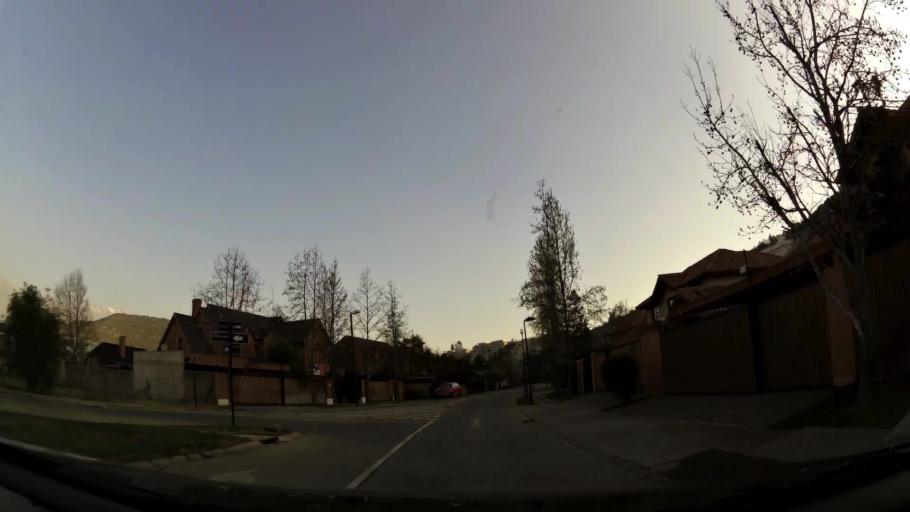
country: CL
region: Santiago Metropolitan
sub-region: Provincia de Santiago
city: Villa Presidente Frei, Nunoa, Santiago, Chile
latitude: -33.3580
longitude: -70.5457
